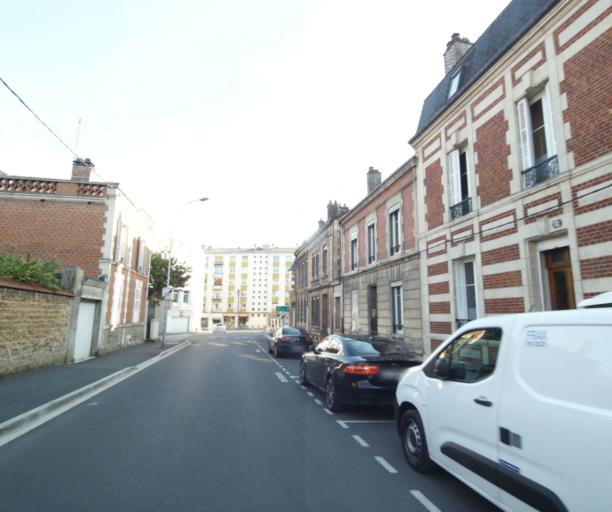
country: FR
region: Champagne-Ardenne
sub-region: Departement des Ardennes
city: Charleville-Mezieres
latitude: 49.7689
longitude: 4.7161
